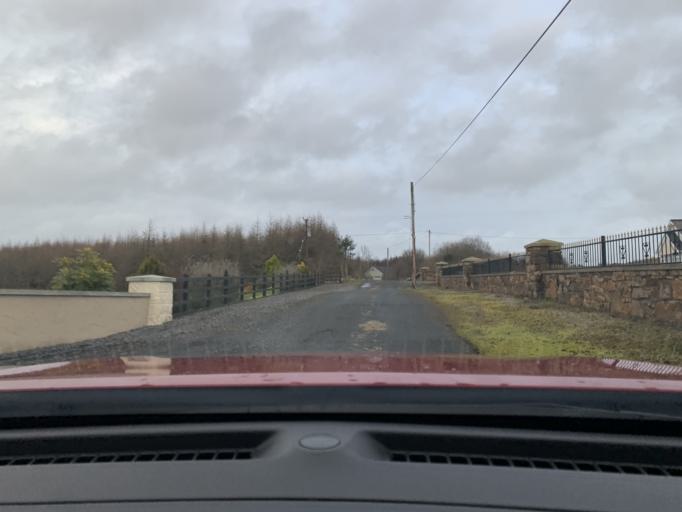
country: IE
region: Connaught
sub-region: Roscommon
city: Boyle
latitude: 53.9836
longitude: -8.4228
